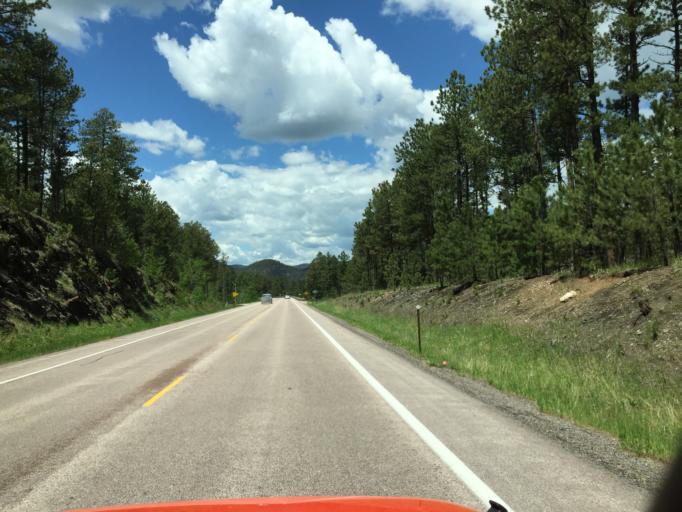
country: US
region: South Dakota
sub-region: Custer County
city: Custer
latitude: 43.8959
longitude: -103.5747
